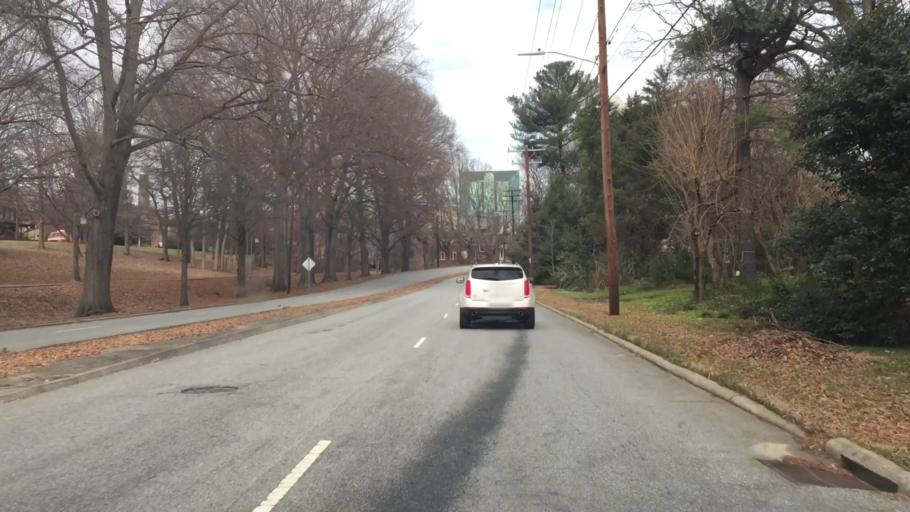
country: US
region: North Carolina
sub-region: Forsyth County
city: Winston-Salem
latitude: 36.0882
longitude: -80.2438
